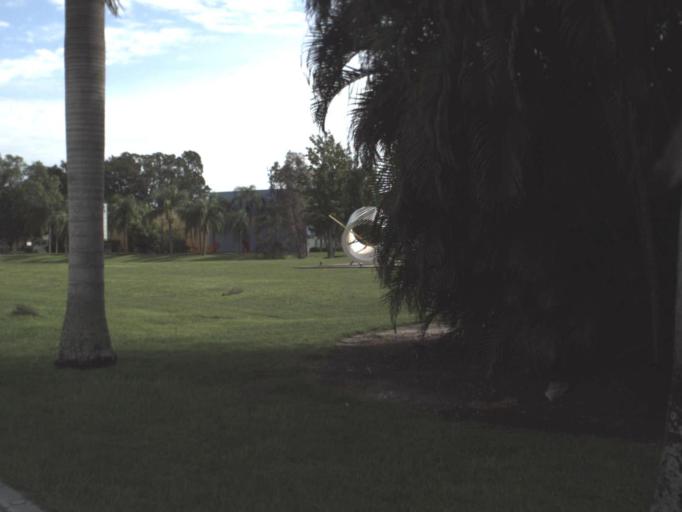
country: US
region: Florida
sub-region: Lee County
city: Whiskey Creek
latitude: 26.5940
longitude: -81.8918
